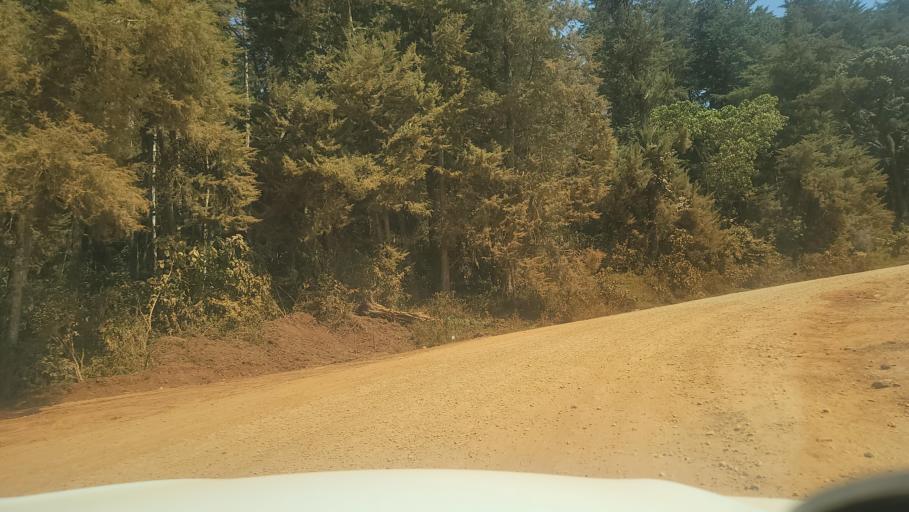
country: ET
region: Oromiya
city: Agaro
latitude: 7.7855
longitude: 36.4092
